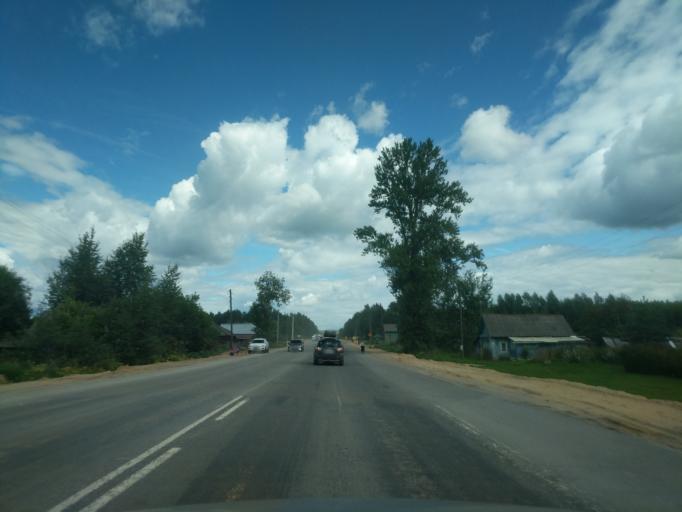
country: RU
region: Jaroslavl
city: Levashevo
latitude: 57.6563
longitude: 40.5635
